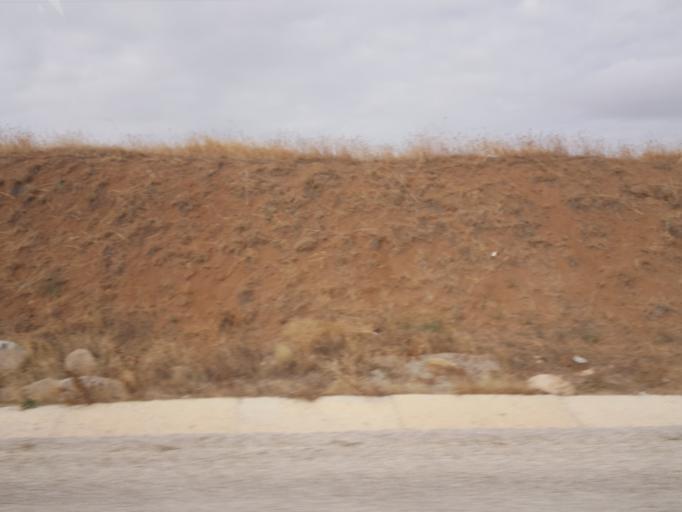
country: TR
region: Kirikkale
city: Bahsili
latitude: 39.7089
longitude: 33.4271
